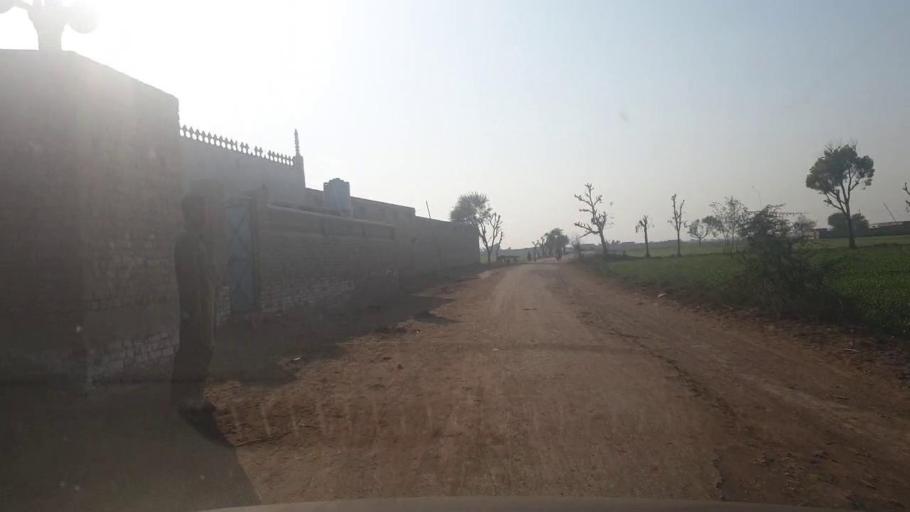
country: PK
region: Sindh
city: Sakrand
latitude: 26.0532
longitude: 68.3925
